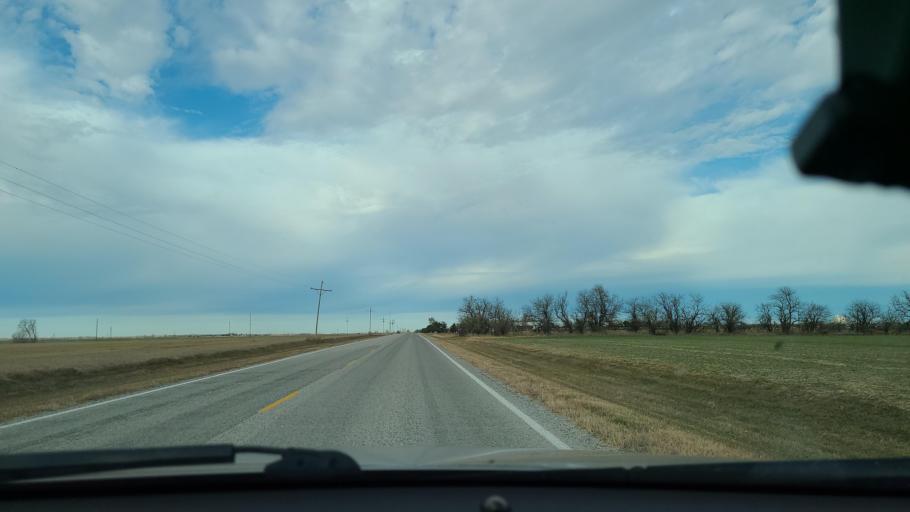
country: US
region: Kansas
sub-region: McPherson County
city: Inman
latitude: 38.3649
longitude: -97.9245
